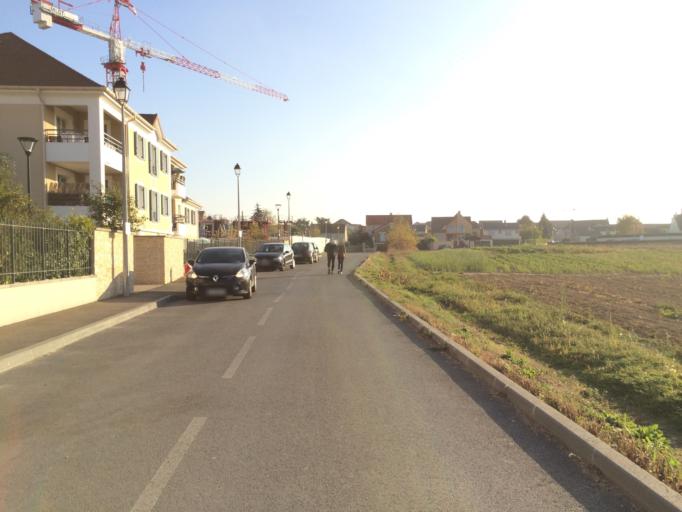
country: FR
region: Ile-de-France
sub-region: Departement de l'Essonne
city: Nozay
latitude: 48.6631
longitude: 2.2419
